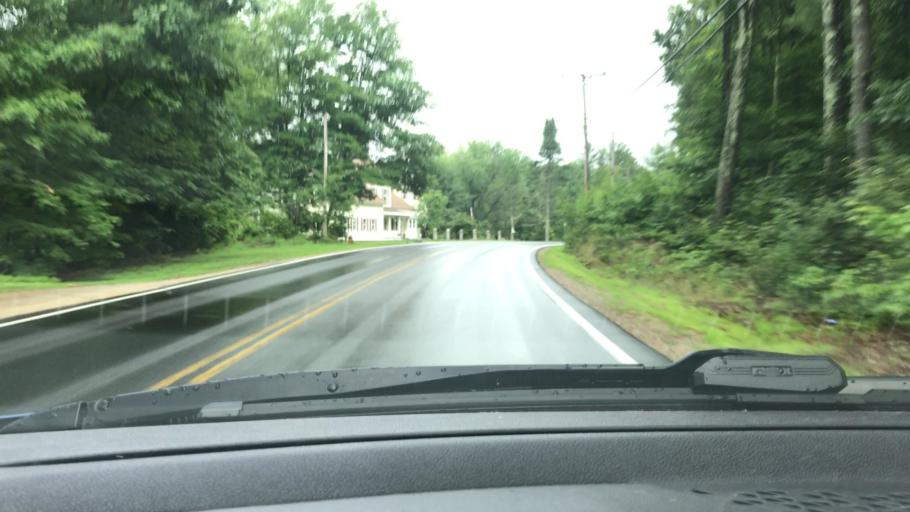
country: US
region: New Hampshire
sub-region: Rockingham County
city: Candia
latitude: 43.1555
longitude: -71.2361
